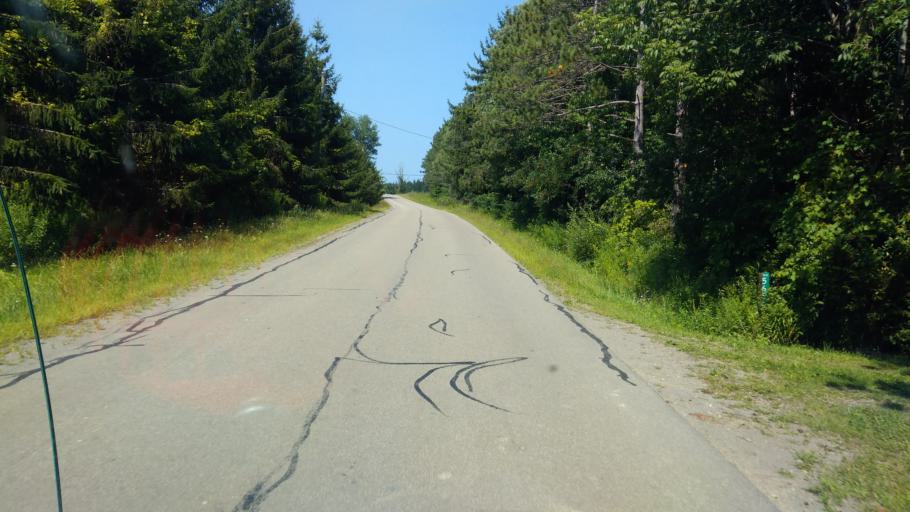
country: US
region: New York
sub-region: Allegany County
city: Belmont
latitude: 42.3091
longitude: -78.0571
